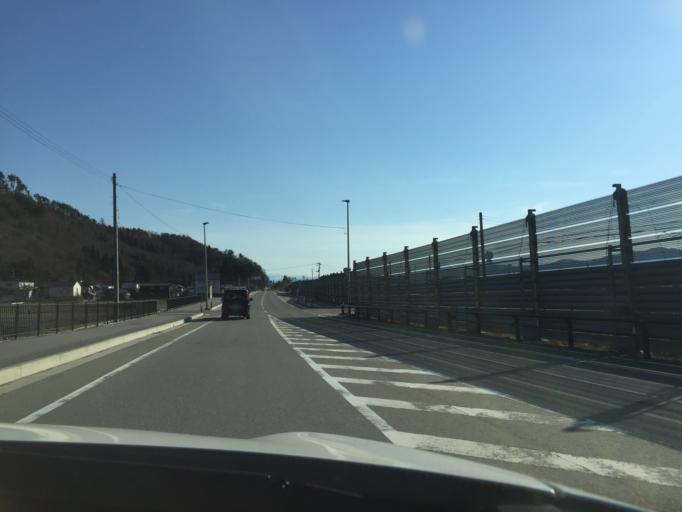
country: JP
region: Yamagata
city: Nagai
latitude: 38.1256
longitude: 140.0560
